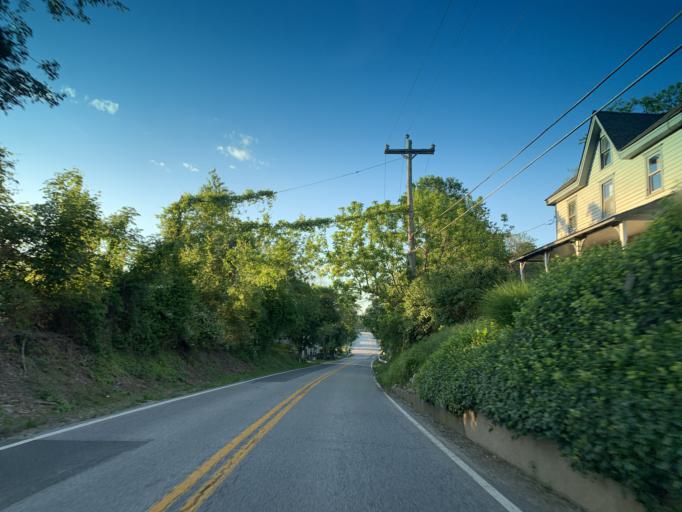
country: US
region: Maryland
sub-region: Cecil County
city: Elkton
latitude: 39.7044
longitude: -75.8683
